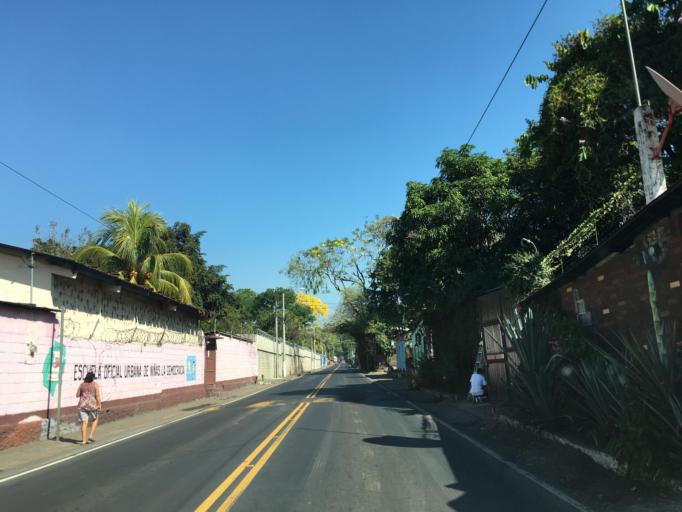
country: GT
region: Escuintla
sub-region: Municipio de La Democracia
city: La Democracia
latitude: 14.2302
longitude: -90.9494
